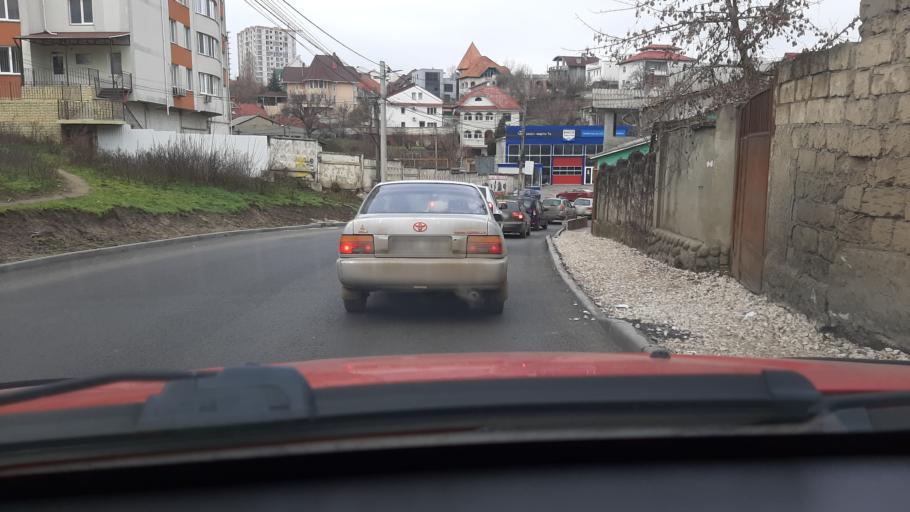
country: MD
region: Chisinau
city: Chisinau
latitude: 47.0048
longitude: 28.8372
